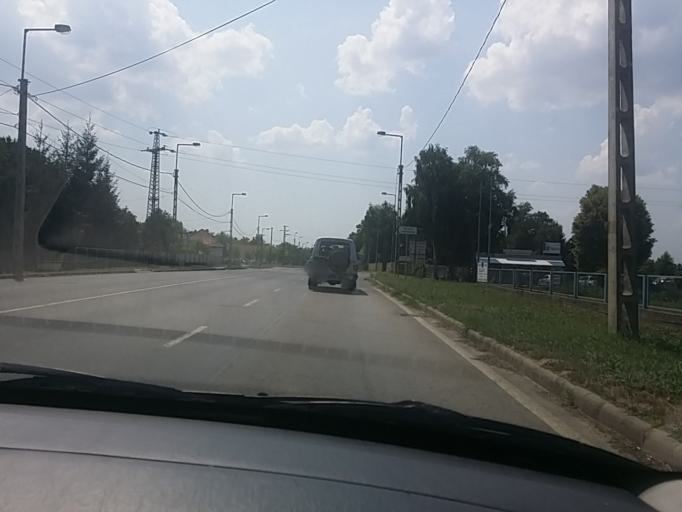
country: HU
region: Tolna
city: Dombovar
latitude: 46.3902
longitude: 18.1440
